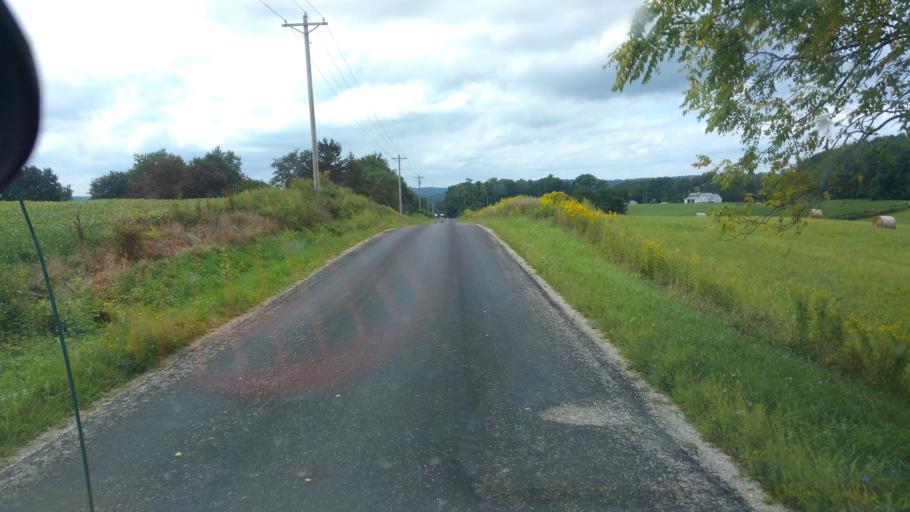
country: US
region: Ohio
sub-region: Ashland County
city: Ashland
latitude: 40.8220
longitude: -82.3828
